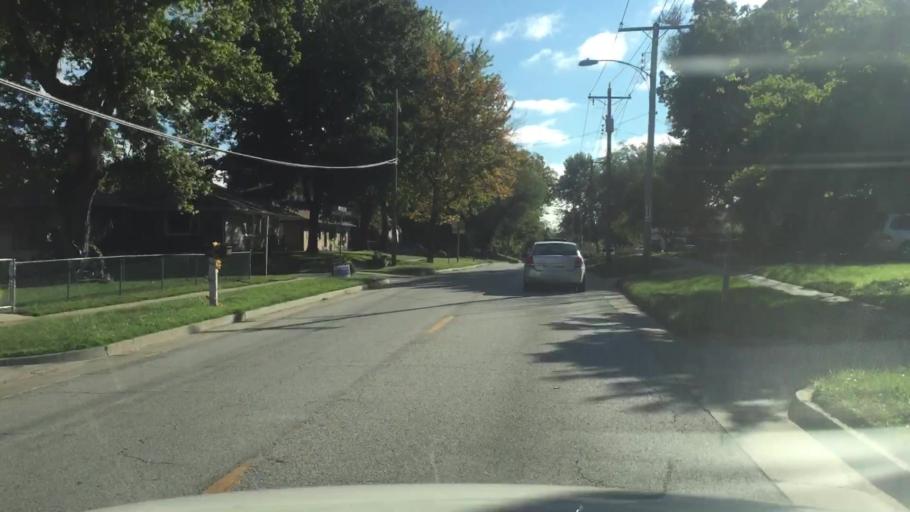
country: US
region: Missouri
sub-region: Howard County
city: New Franklin
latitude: 39.0175
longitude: -92.7405
